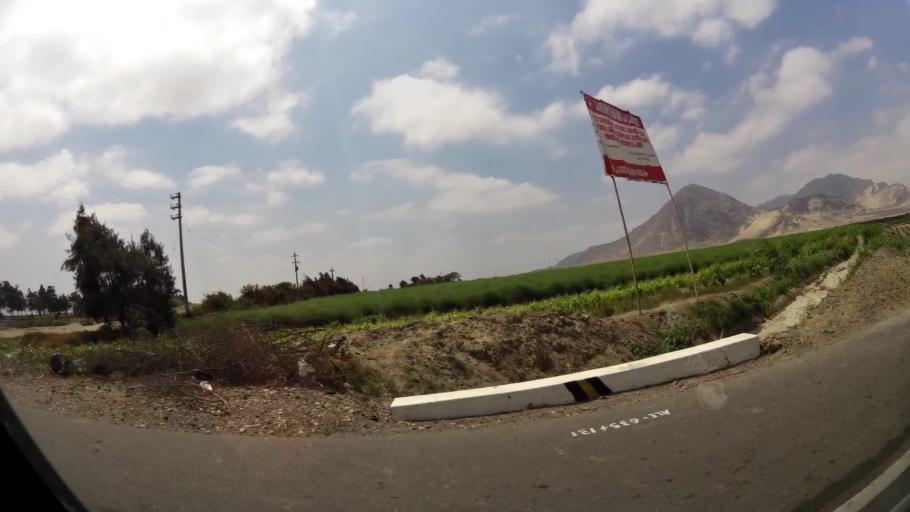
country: PE
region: La Libertad
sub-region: Ascope
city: Paijan
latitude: -7.6717
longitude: -79.3270
